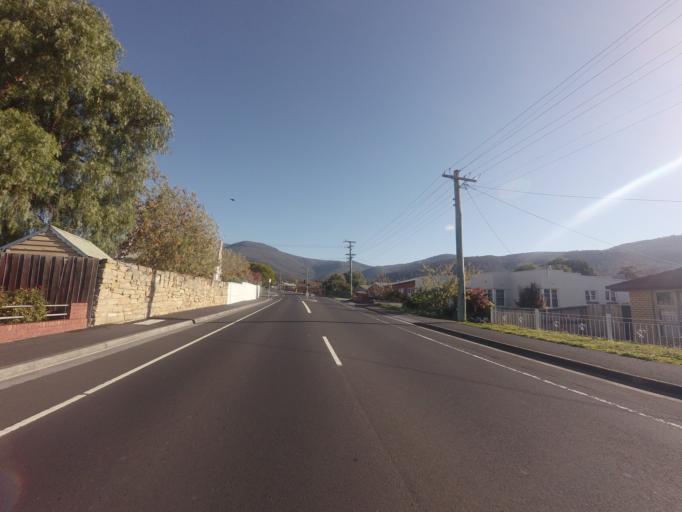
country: AU
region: Tasmania
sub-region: Glenorchy
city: Glenorchy
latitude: -42.8434
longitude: 147.2672
